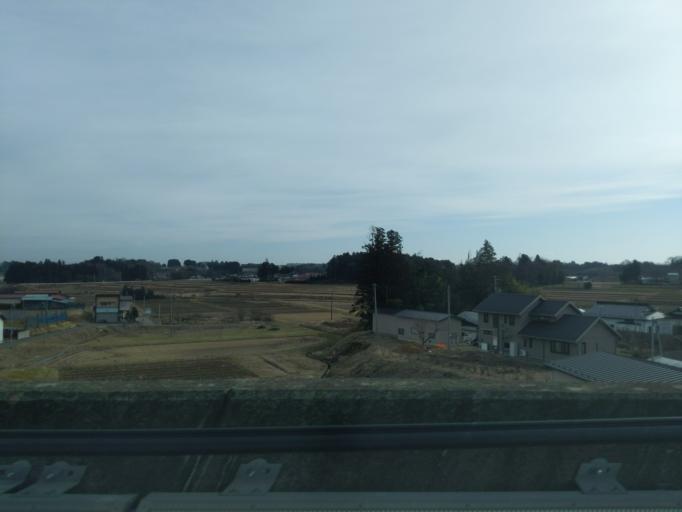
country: JP
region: Iwate
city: Ichinoseki
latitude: 38.7452
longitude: 141.0697
